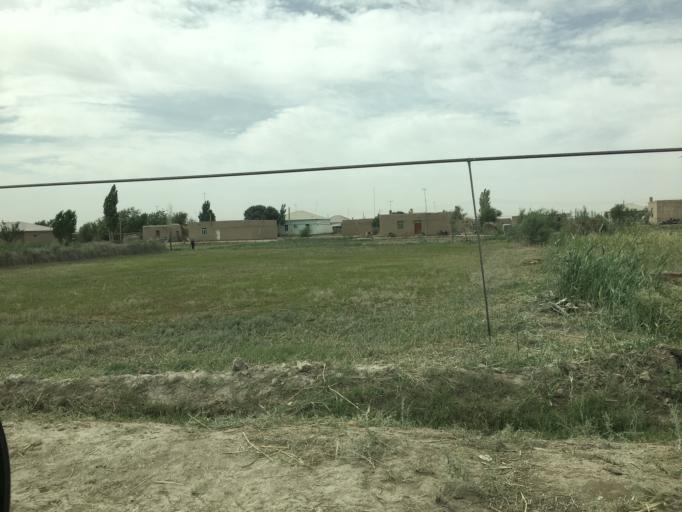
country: TM
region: Dasoguz
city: Tagta
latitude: 41.5400
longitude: 59.8072
